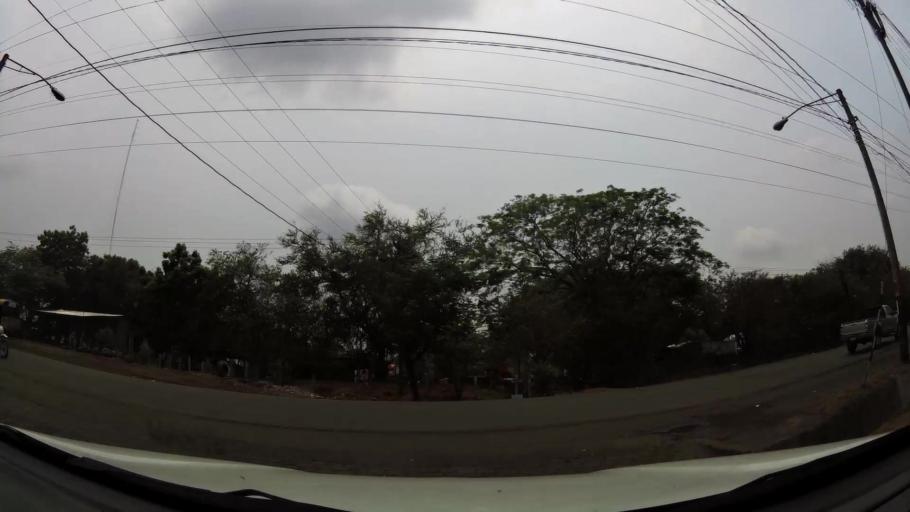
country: NI
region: Chinandega
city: Chinandega
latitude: 12.6317
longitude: -87.1186
